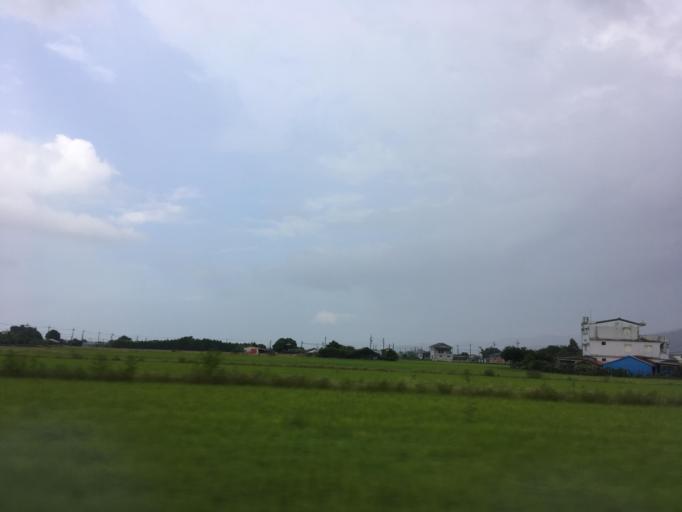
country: TW
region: Taiwan
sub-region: Yilan
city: Yilan
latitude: 24.6713
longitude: 121.6355
